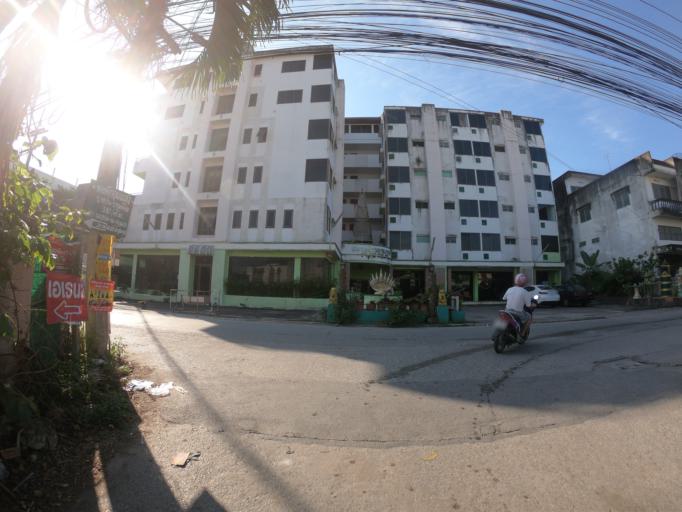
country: TH
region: Chiang Mai
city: Chiang Mai
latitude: 18.7985
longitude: 98.9837
